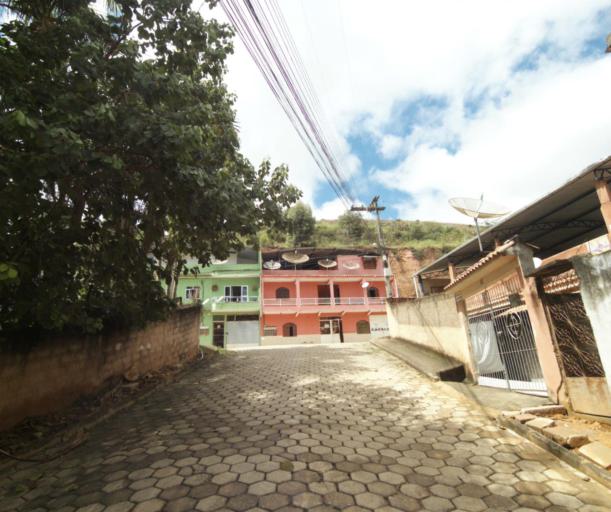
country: BR
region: Espirito Santo
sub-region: Irupi
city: Irupi
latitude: -20.3488
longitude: -41.6460
